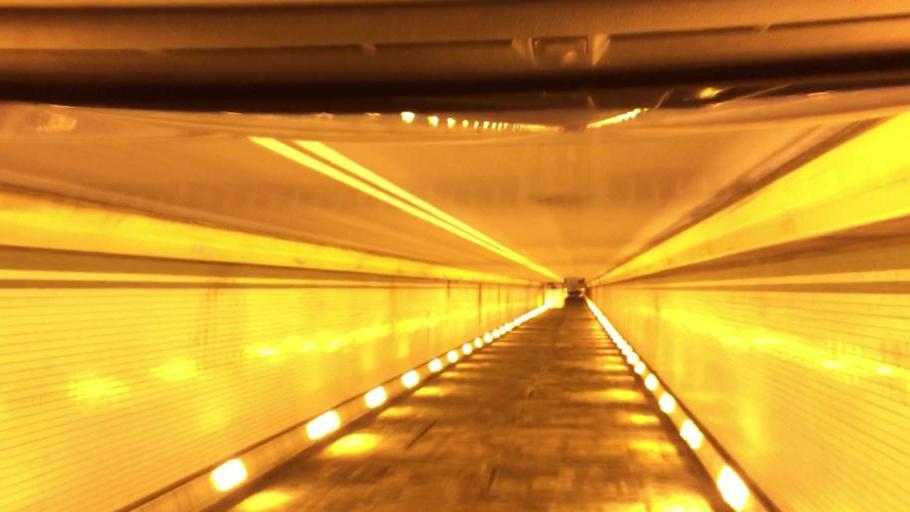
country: US
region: Pennsylvania
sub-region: Franklin County
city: Doylestown
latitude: 40.1562
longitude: -77.6765
